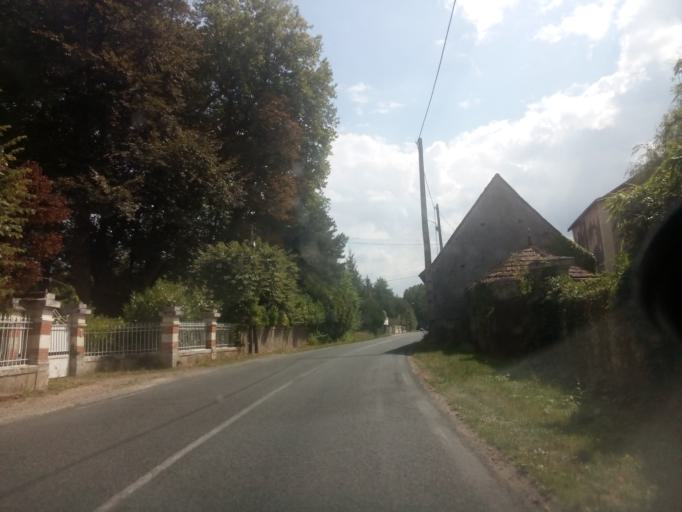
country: FR
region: Centre
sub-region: Departement d'Indre-et-Loire
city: Azay-le-Rideau
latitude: 47.2670
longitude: 0.4402
